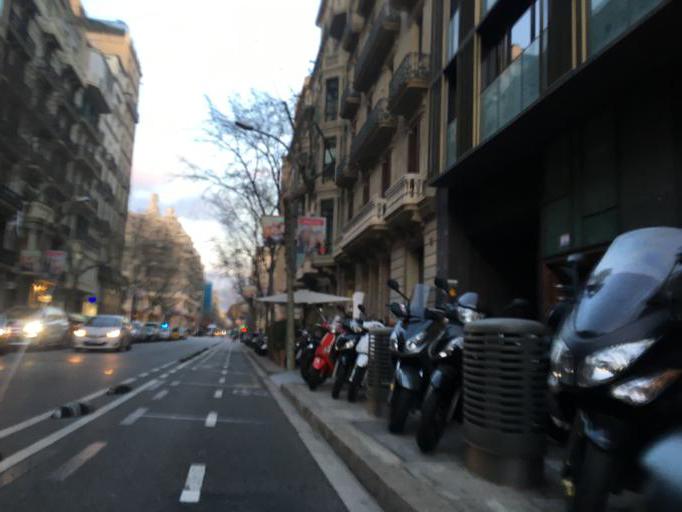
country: ES
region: Catalonia
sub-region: Provincia de Barcelona
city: Eixample
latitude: 41.3938
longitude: 2.1603
